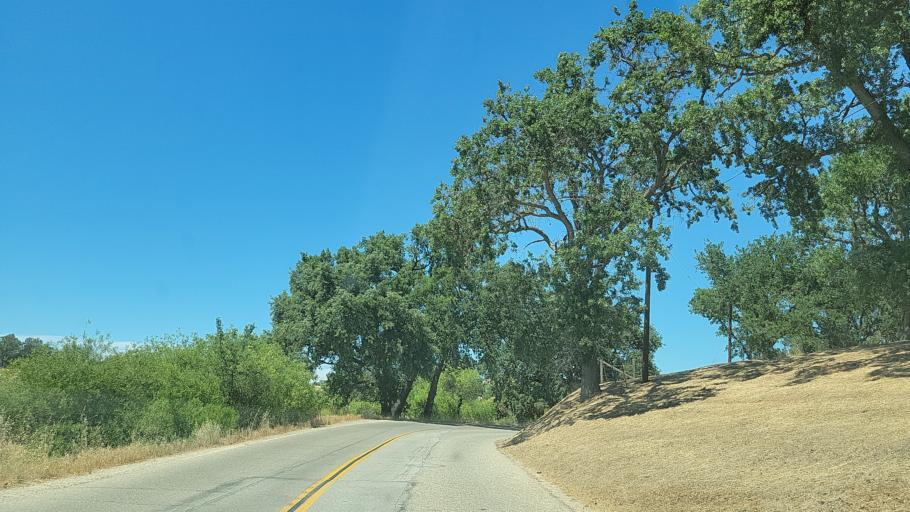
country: US
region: California
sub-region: San Luis Obispo County
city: Atascadero
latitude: 35.4559
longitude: -120.6319
